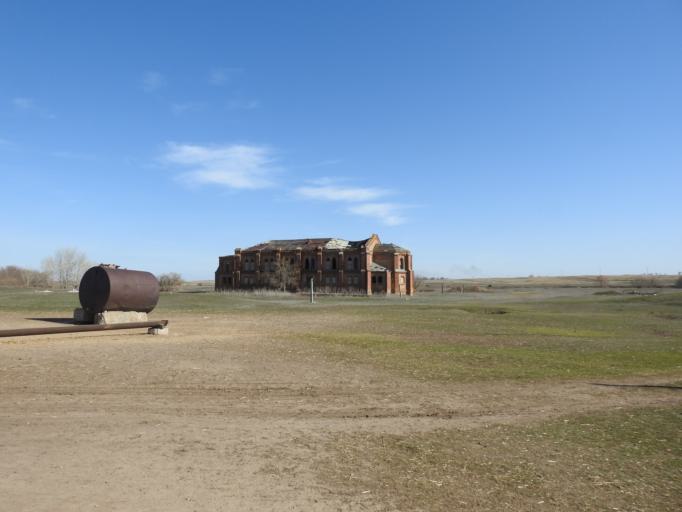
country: RU
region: Volgograd
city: Staraya Poltavka
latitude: 50.7795
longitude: 46.4144
